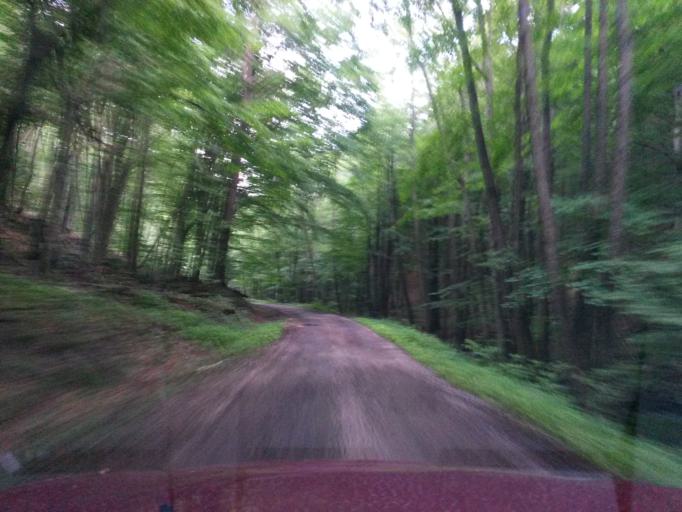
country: SK
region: Kosicky
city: Moldava nad Bodvou
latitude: 48.7345
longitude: 21.0647
